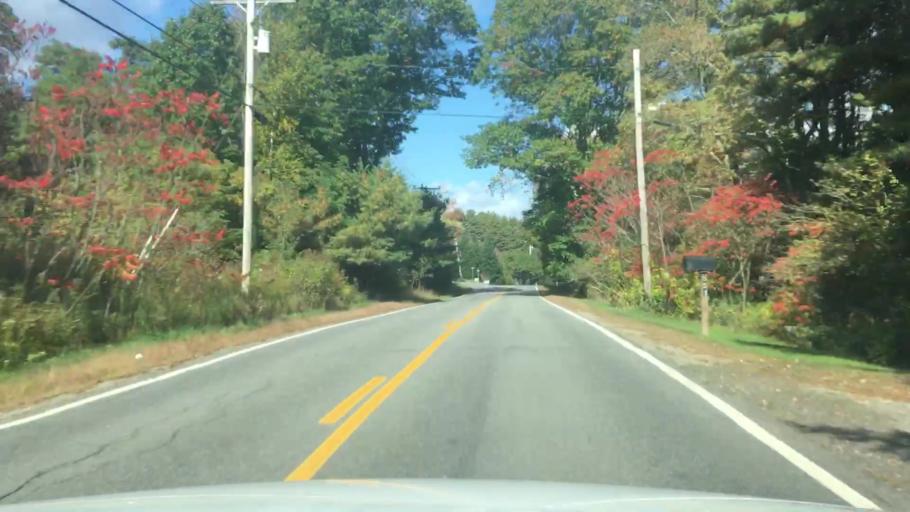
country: US
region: Maine
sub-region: Knox County
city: Union
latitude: 44.2322
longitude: -69.2818
